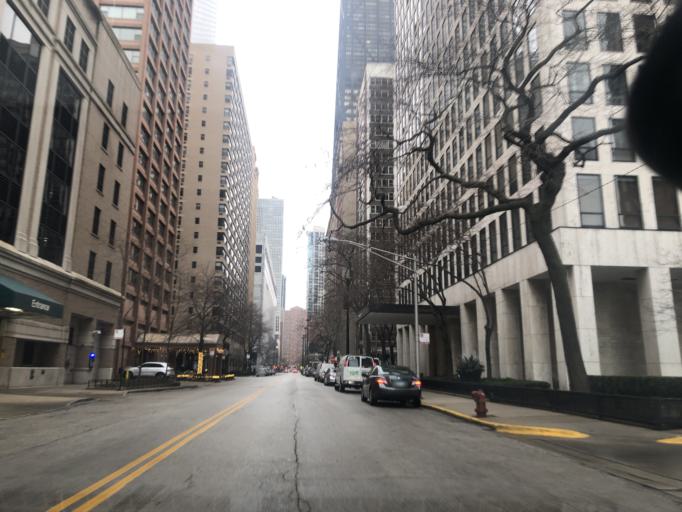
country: US
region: Illinois
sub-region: Cook County
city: Chicago
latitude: 41.8985
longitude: -87.6192
